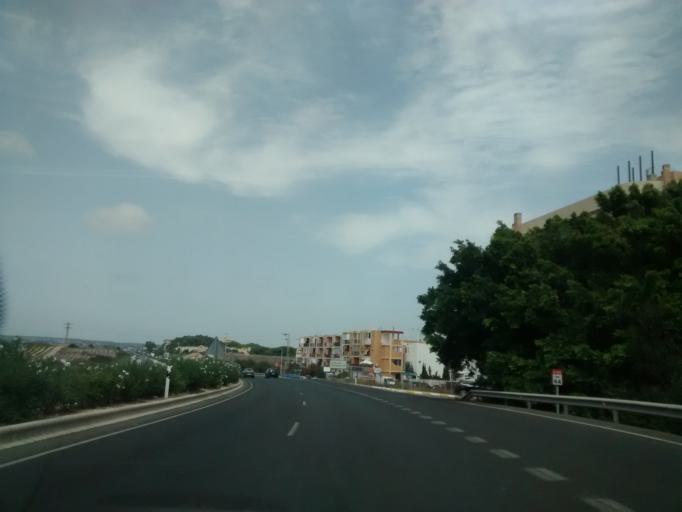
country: ES
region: Valencia
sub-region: Provincia de Alicante
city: Torrevieja
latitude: 38.0268
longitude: -0.6560
